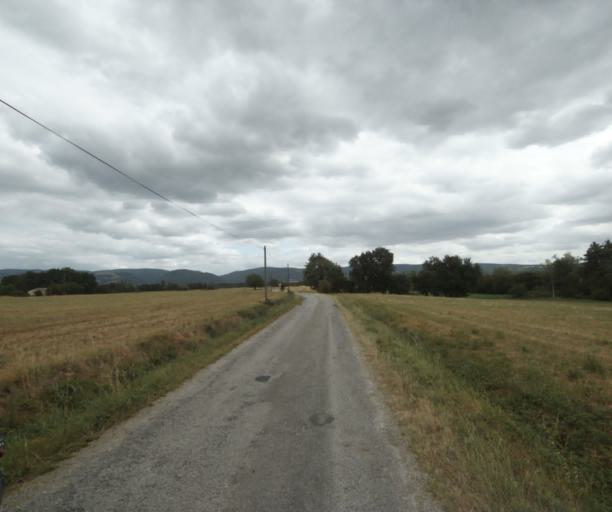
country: FR
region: Midi-Pyrenees
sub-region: Departement de la Haute-Garonne
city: Revel
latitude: 43.4846
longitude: 2.0284
